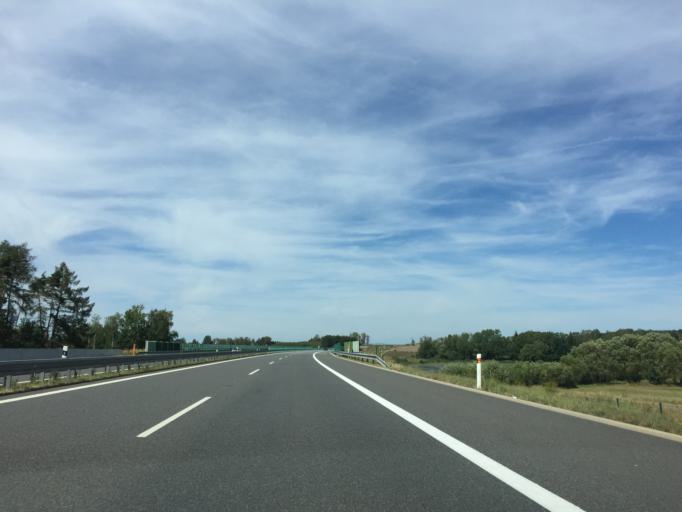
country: CZ
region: Jihocesky
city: Sobeslav
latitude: 49.2895
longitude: 14.7348
